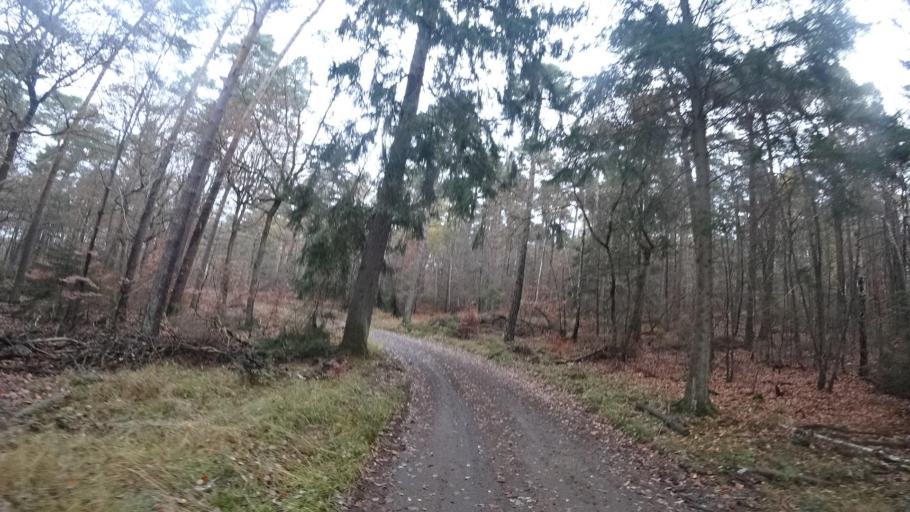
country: DE
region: Rheinland-Pfalz
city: Schalkenbach
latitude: 50.4990
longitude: 7.1192
